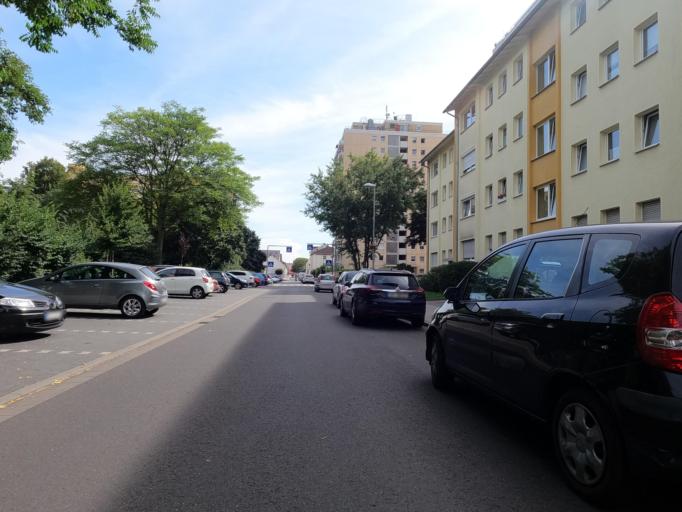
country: DE
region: Hesse
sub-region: Regierungsbezirk Darmstadt
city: Neu Isenburg
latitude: 50.0537
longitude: 8.6970
